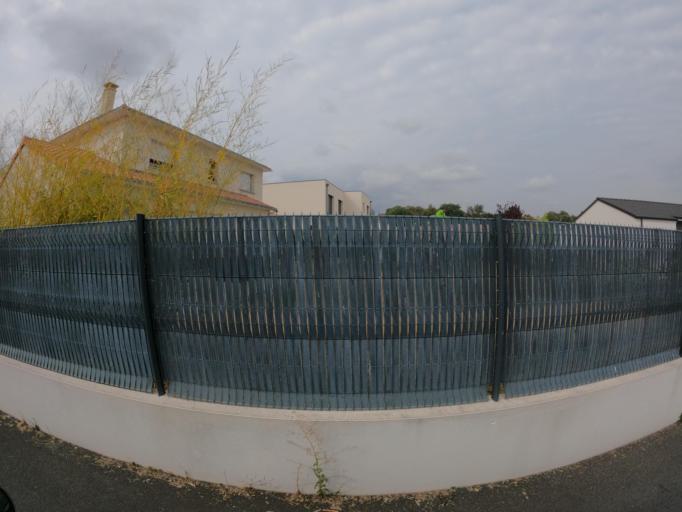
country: FR
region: Pays de la Loire
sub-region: Departement de Maine-et-Loire
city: La Seguiniere
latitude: 47.0622
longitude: -0.9301
